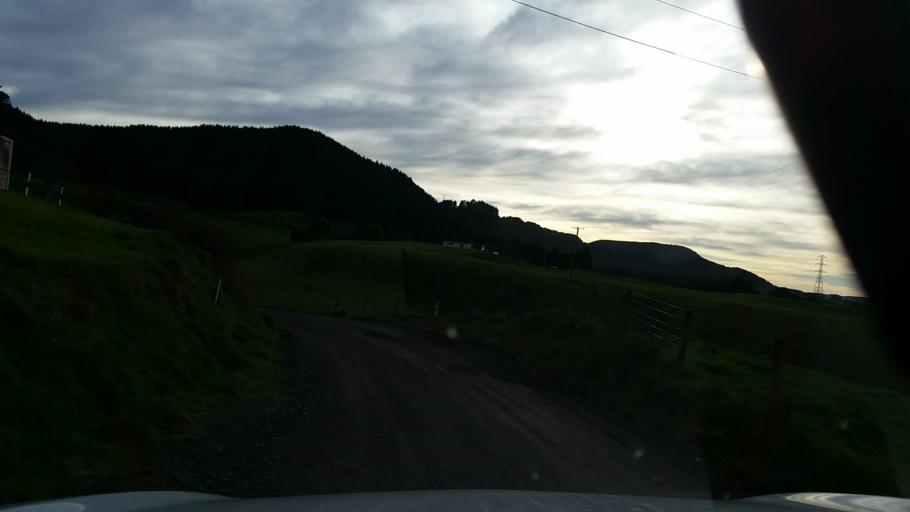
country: NZ
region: Bay of Plenty
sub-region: Rotorua District
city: Rotorua
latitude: -38.2299
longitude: 176.1598
